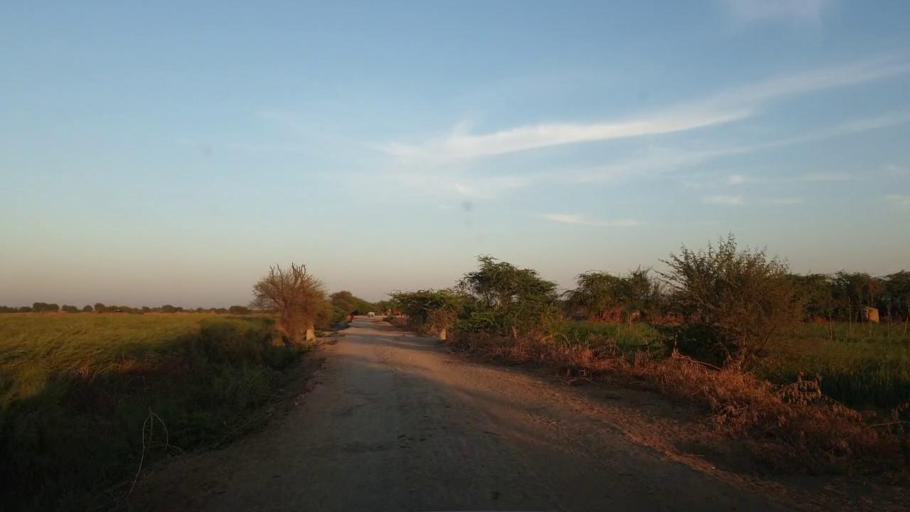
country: PK
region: Sindh
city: Kunri
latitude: 25.1375
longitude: 69.4416
